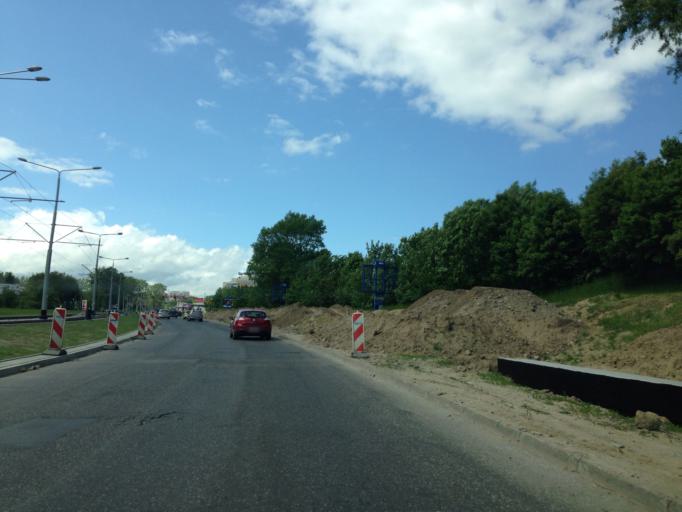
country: PL
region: Pomeranian Voivodeship
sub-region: Gdansk
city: Gdansk
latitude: 54.3496
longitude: 18.6005
